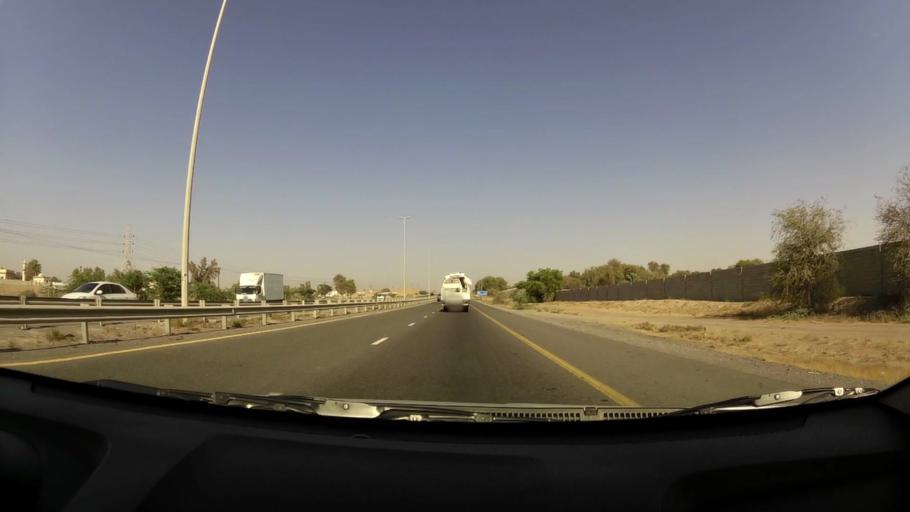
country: AE
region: Umm al Qaywayn
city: Umm al Qaywayn
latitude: 25.4433
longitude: 55.6314
